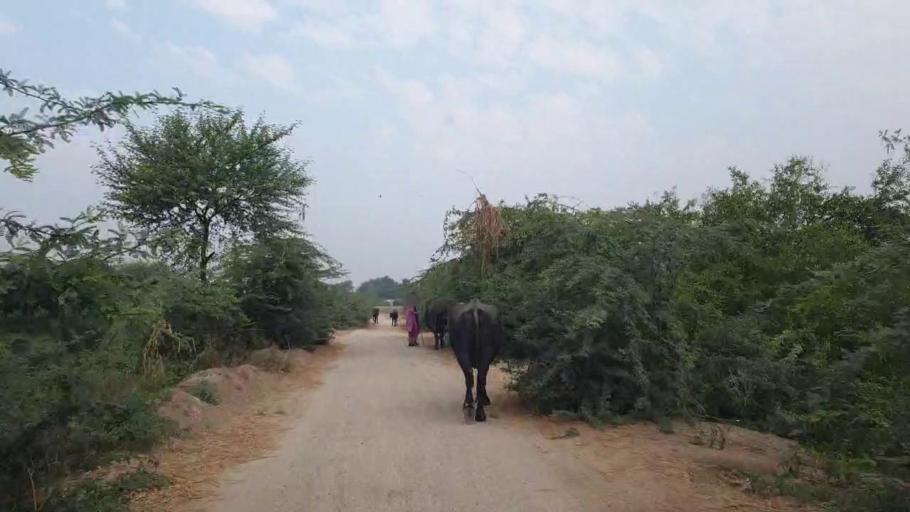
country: PK
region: Sindh
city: Talhar
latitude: 24.8373
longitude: 68.8794
